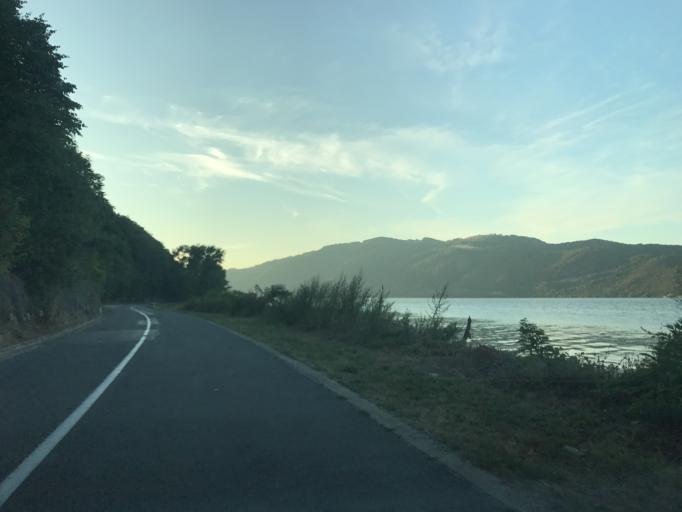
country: RS
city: Radenka
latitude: 44.6484
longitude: 21.8071
